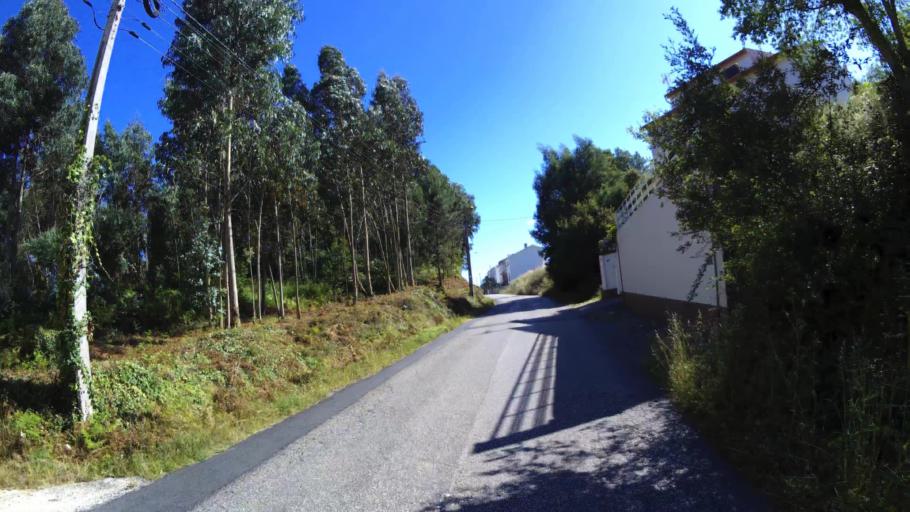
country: PT
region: Aveiro
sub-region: Aveiro
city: Aveiro
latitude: 40.6623
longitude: -8.6207
